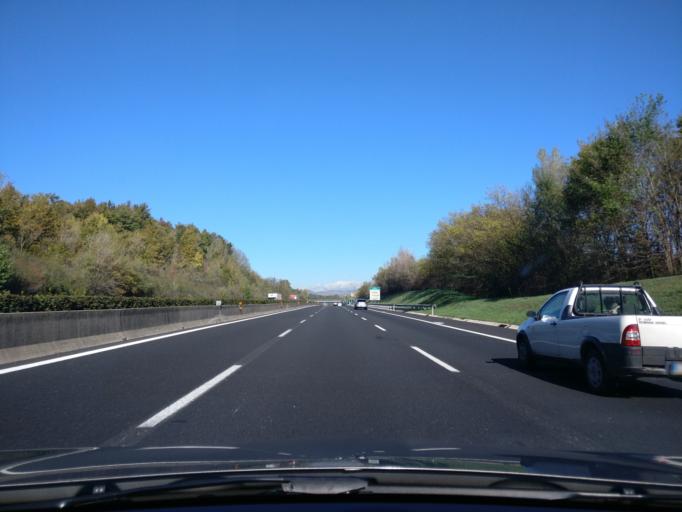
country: IT
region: Latium
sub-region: Provincia di Frosinone
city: Ceccano
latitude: 41.6046
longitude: 13.3327
